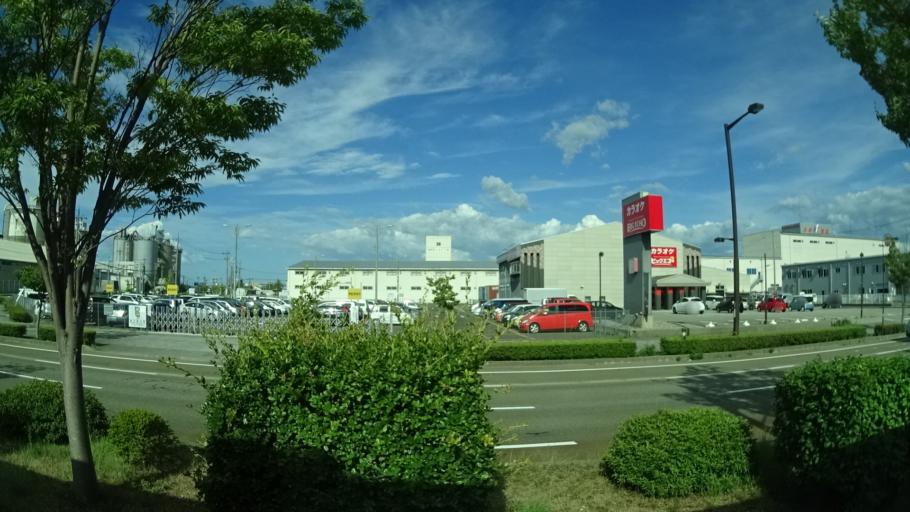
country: JP
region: Ishikawa
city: Kanazawa-shi
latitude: 36.6066
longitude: 136.6183
